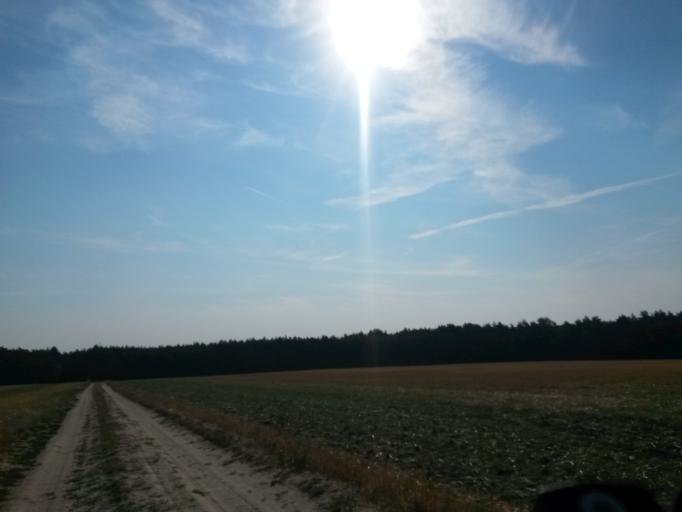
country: DE
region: Saxony-Anhalt
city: Nudersdorf
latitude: 51.9050
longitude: 12.5930
